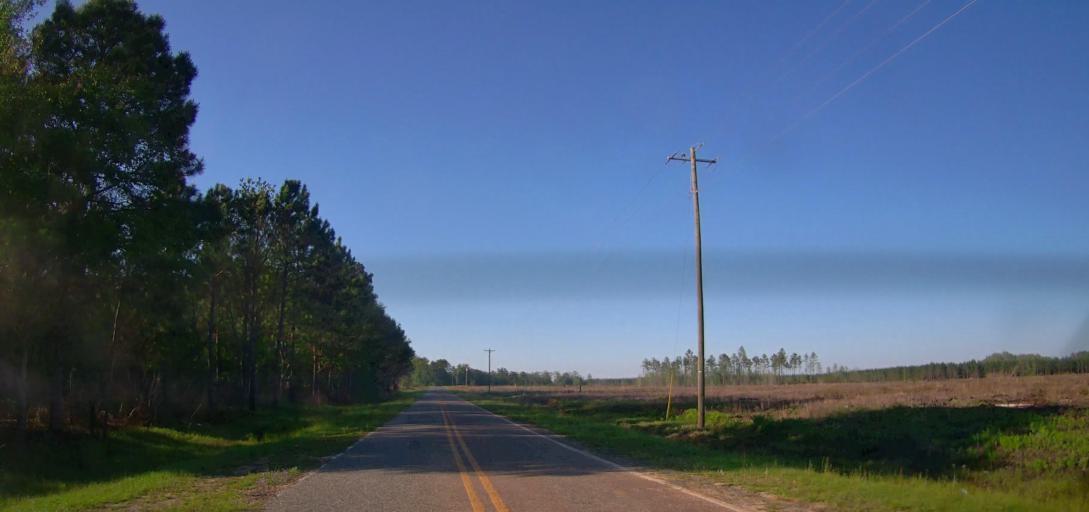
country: US
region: Georgia
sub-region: Ben Hill County
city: Fitzgerald
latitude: 31.6784
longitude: -83.1466
